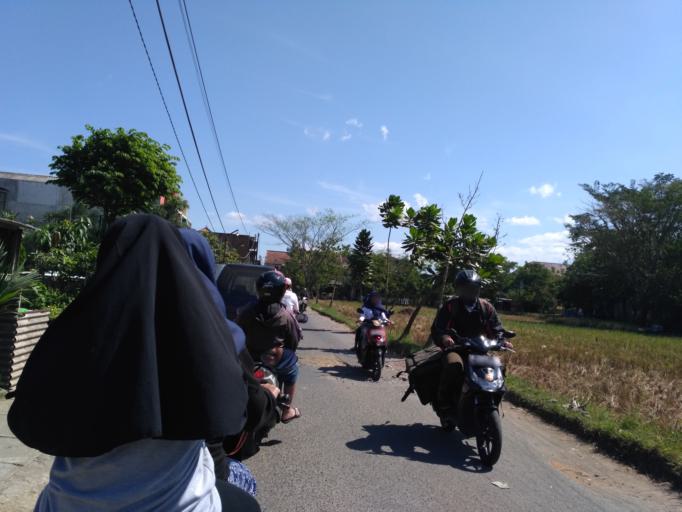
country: ID
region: East Java
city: Malang
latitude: -7.9731
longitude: 112.6678
